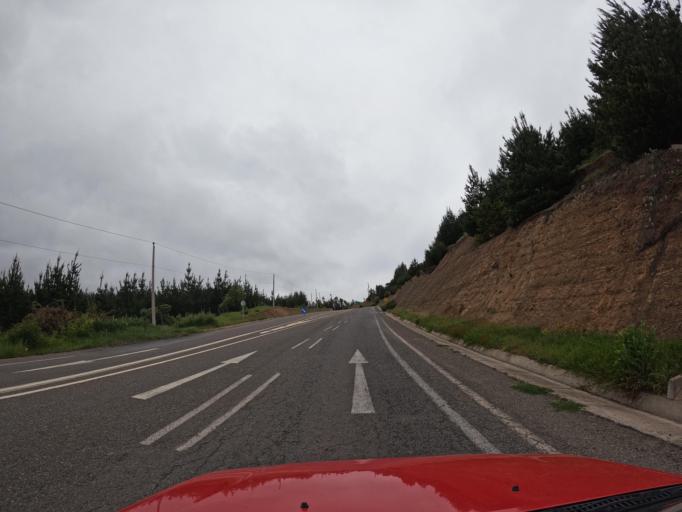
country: CL
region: O'Higgins
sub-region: Provincia de Colchagua
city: Santa Cruz
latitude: -34.6320
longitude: -72.0179
